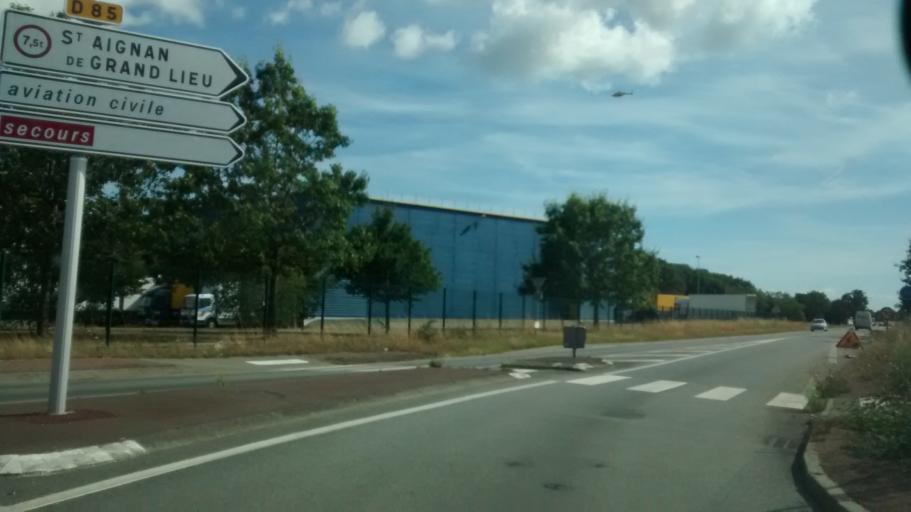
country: FR
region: Pays de la Loire
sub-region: Departement de la Loire-Atlantique
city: Pont-Saint-Martin
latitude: 47.1523
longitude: -1.6001
